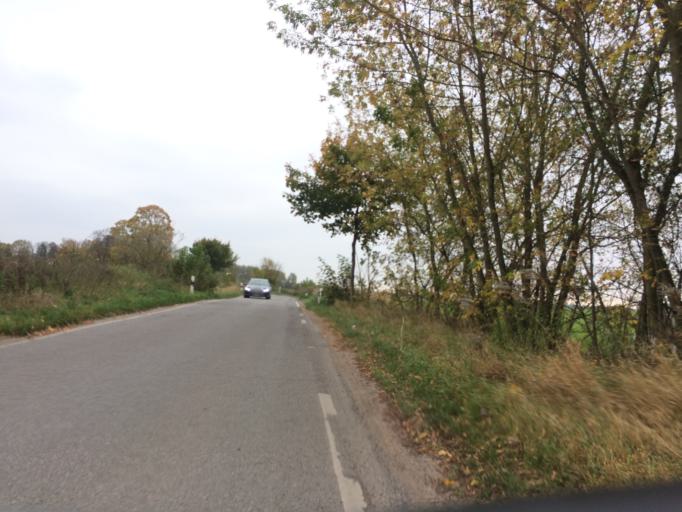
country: DE
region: Berlin
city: Blankenfelde
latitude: 52.6164
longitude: 13.3999
